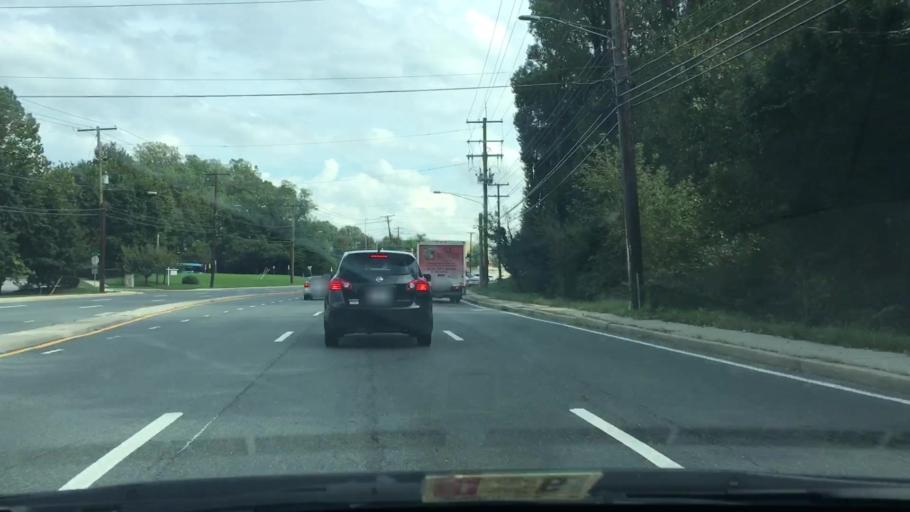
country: US
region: Maryland
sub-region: Montgomery County
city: Kemp Mill
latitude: 39.0360
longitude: -77.0278
